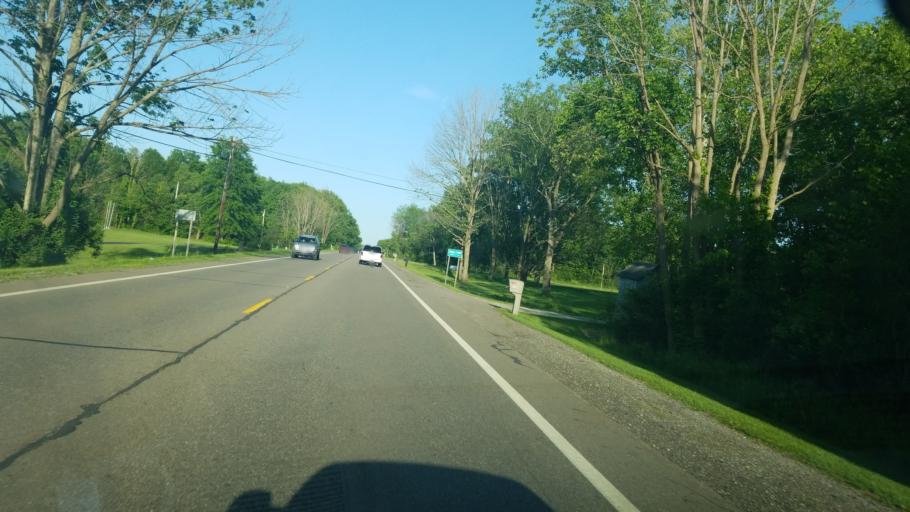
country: US
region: Ohio
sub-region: Portage County
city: Ravenna
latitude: 41.1539
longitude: -81.1934
